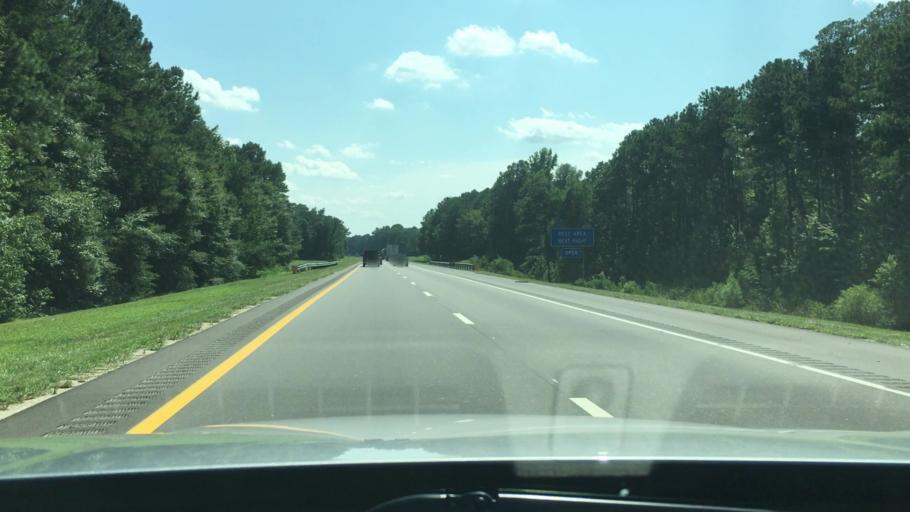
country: US
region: North Carolina
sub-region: Cumberland County
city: Vander
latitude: 34.9989
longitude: -78.8283
